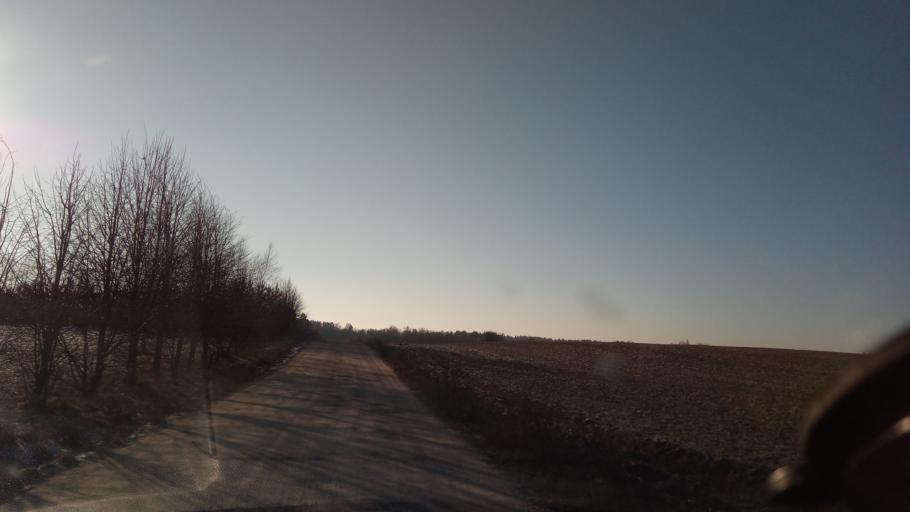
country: LT
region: Alytaus apskritis
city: Druskininkai
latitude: 54.1100
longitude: 24.0129
